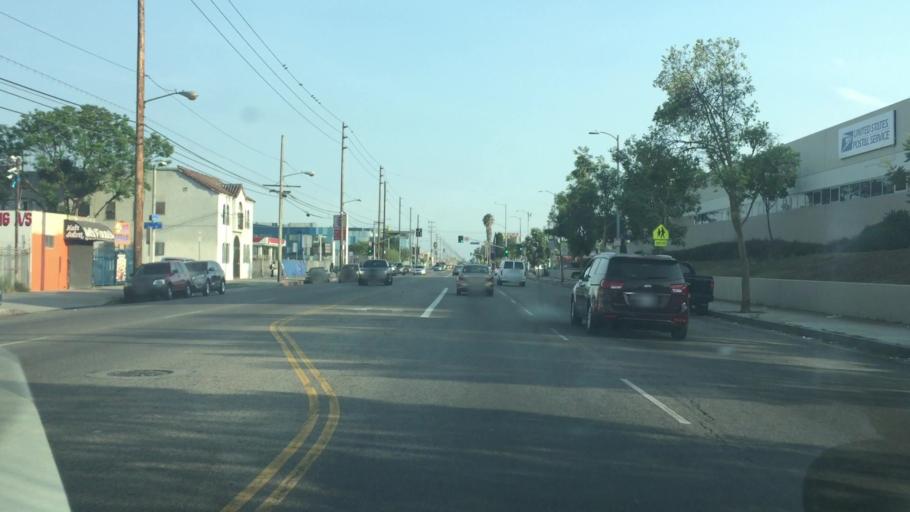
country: US
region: California
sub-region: Los Angeles County
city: Florence-Graham
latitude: 33.9763
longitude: -118.2564
